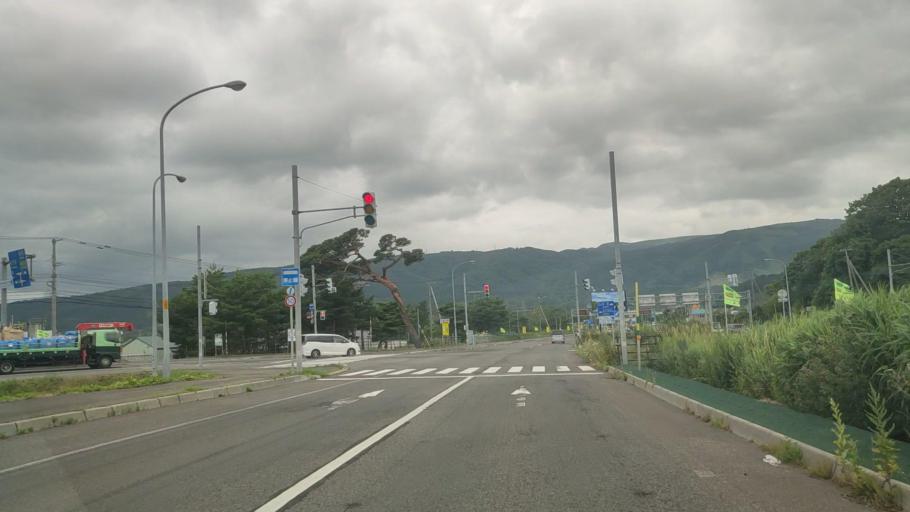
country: JP
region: Hokkaido
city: Nanae
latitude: 41.9229
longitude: 140.6654
